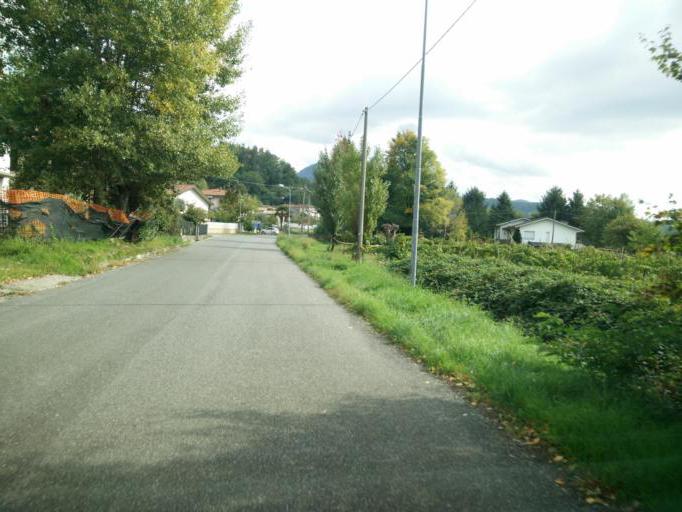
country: IT
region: Tuscany
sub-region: Provincia di Massa-Carrara
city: Villafranca in Lunigiana
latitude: 44.3127
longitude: 9.9663
